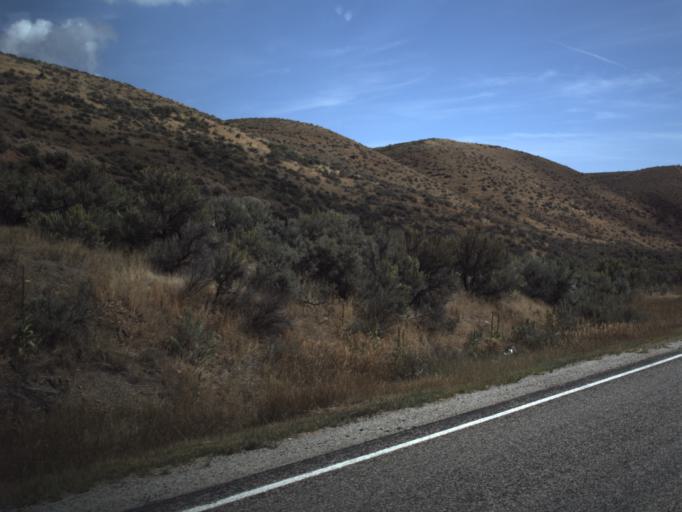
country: US
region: Utah
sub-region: Rich County
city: Randolph
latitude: 41.7826
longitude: -111.2029
